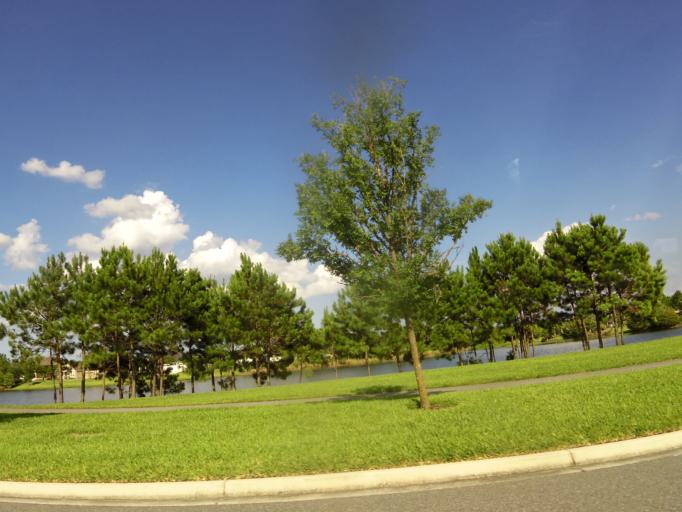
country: US
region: Florida
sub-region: Clay County
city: Green Cove Springs
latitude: 30.0250
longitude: -81.6401
